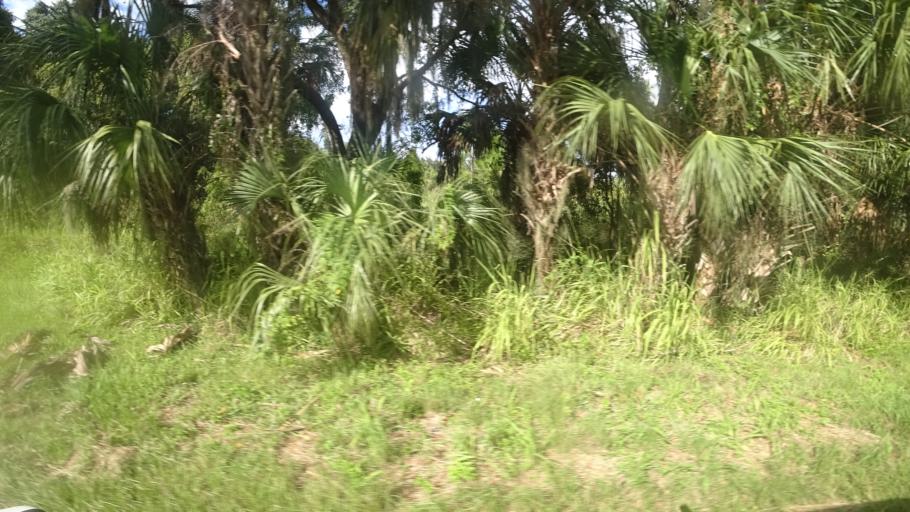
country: US
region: Florida
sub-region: Manatee County
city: Memphis
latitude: 27.6013
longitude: -82.5450
